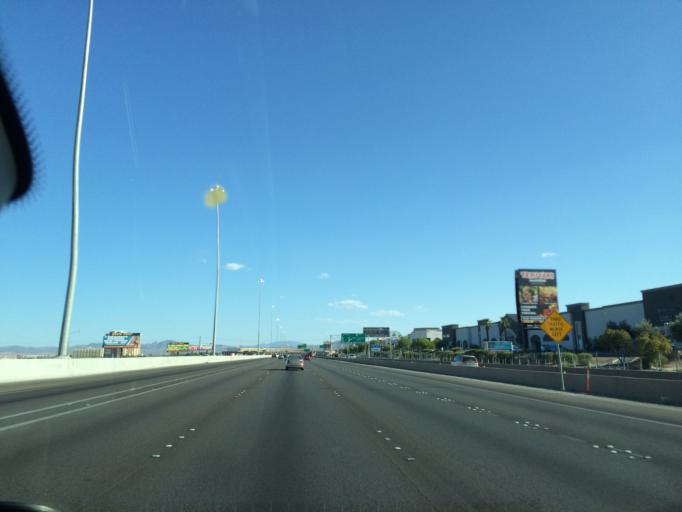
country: US
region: Nevada
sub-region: Clark County
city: Paradise
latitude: 36.0542
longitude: -115.1809
